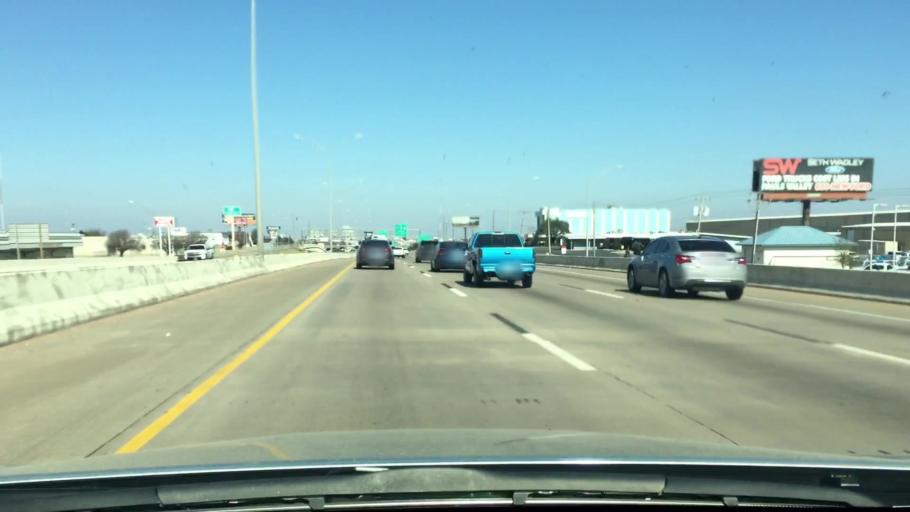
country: US
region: Oklahoma
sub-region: Cleveland County
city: Moore
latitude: 35.3780
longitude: -97.4949
